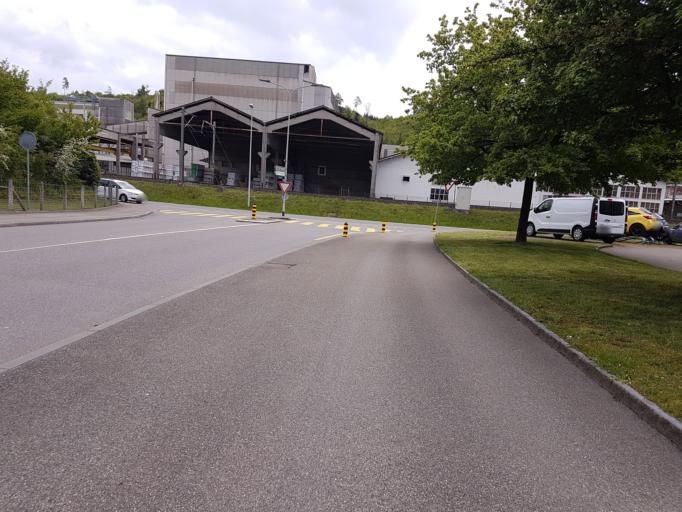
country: CH
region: Aargau
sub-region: Bezirk Brugg
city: Brugg
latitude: 47.4736
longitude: 8.1963
